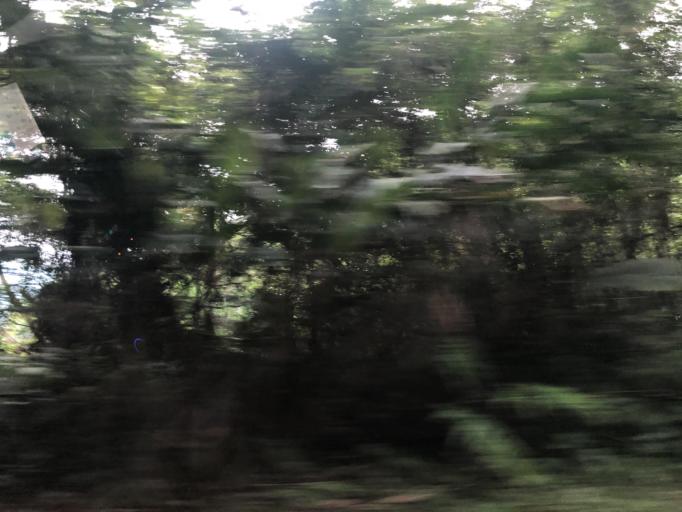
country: TW
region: Taipei
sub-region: Taipei
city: Banqiao
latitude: 24.8907
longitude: 121.4288
